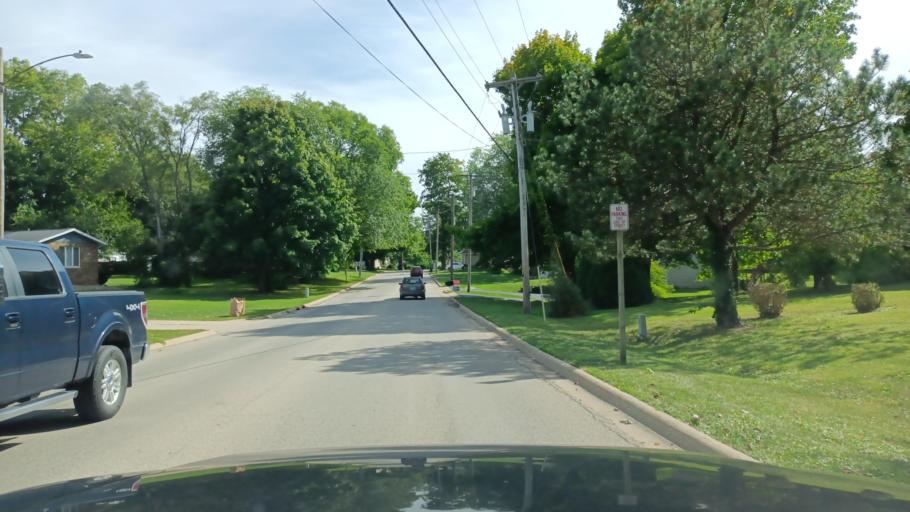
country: US
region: Illinois
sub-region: Knox County
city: Knoxville
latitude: 40.9107
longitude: -90.2901
